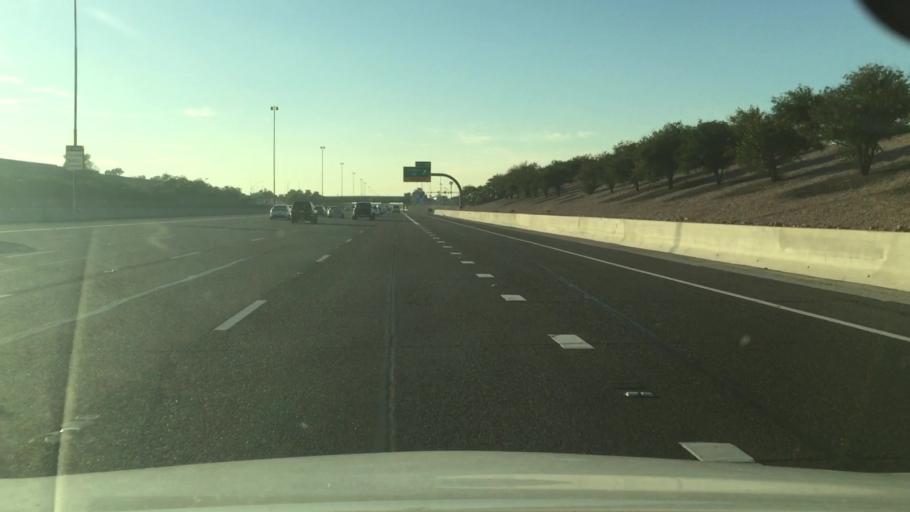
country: US
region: Arizona
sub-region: Maricopa County
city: Gilbert
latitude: 33.3853
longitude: -111.7809
